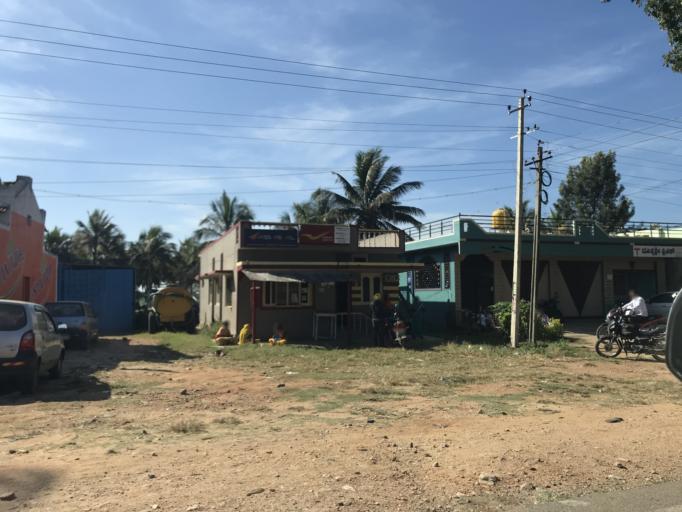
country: IN
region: Karnataka
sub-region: Mysore
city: Sargur
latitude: 12.1217
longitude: 76.4803
